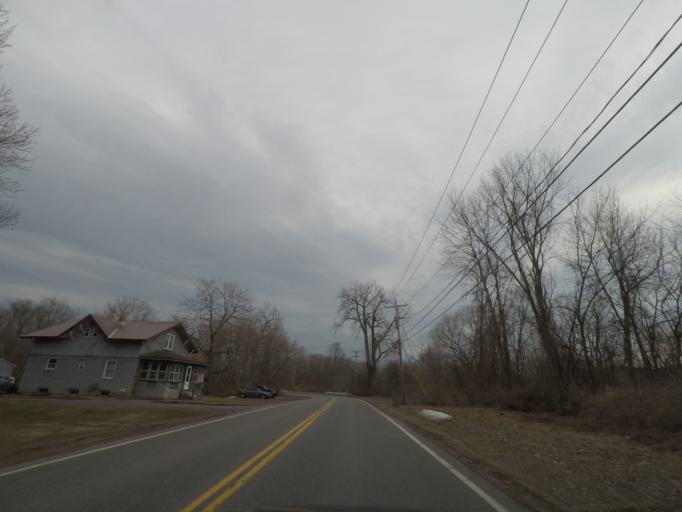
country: US
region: New York
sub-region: Saratoga County
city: Schuylerville
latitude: 43.1256
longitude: -73.5829
